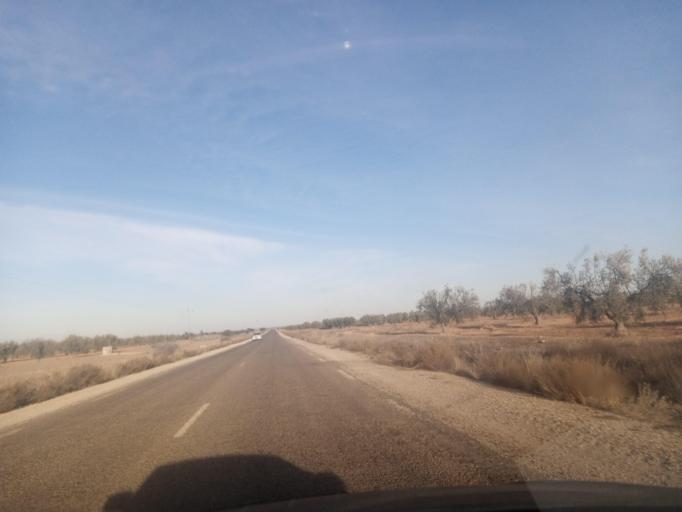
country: TN
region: Safaqis
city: Bi'r `Ali Bin Khalifah
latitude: 34.9334
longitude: 10.3303
